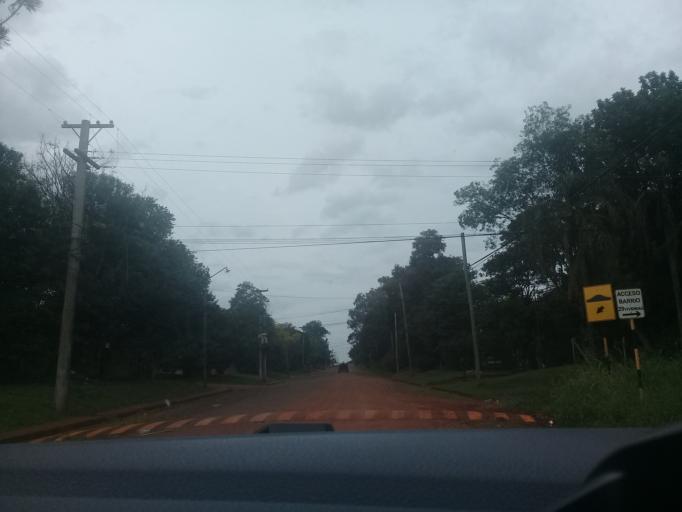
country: AR
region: Misiones
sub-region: Departamento de Obera
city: Obera
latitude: -27.4815
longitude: -55.1527
